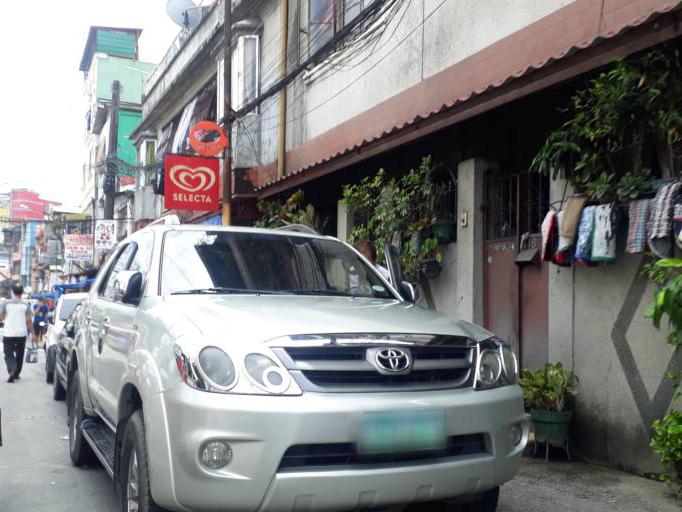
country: PH
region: Metro Manila
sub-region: San Juan
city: San Juan
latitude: 14.6179
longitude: 121.0489
